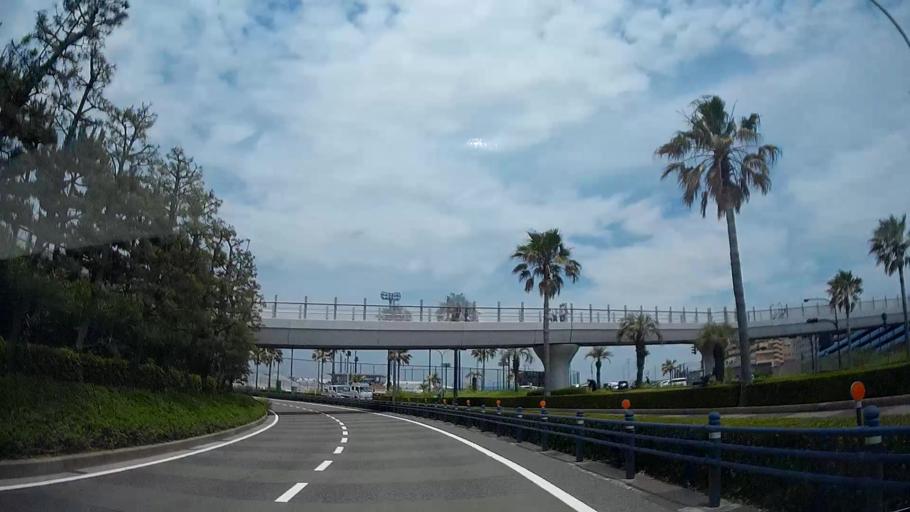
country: JP
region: Tokyo
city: Urayasu
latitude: 35.6257
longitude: 139.8920
